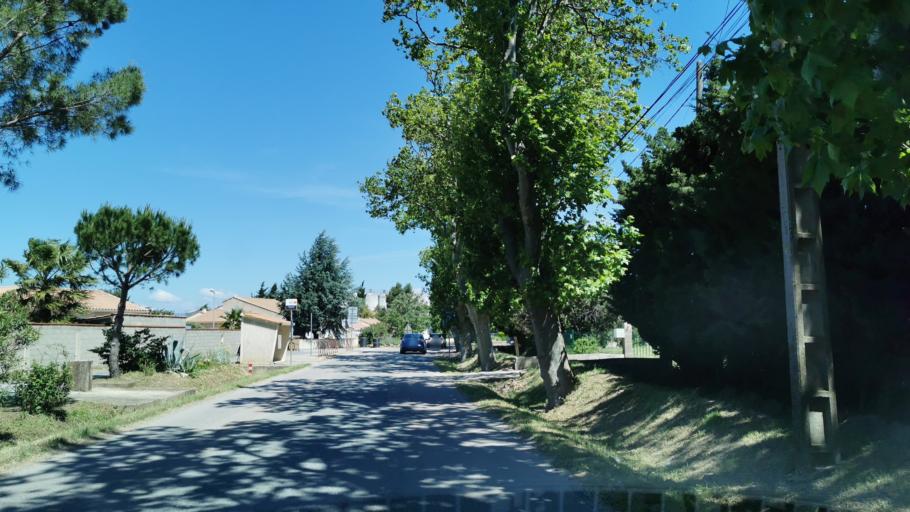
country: FR
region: Languedoc-Roussillon
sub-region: Departement de l'Aude
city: Canet
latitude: 43.2205
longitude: 2.8459
